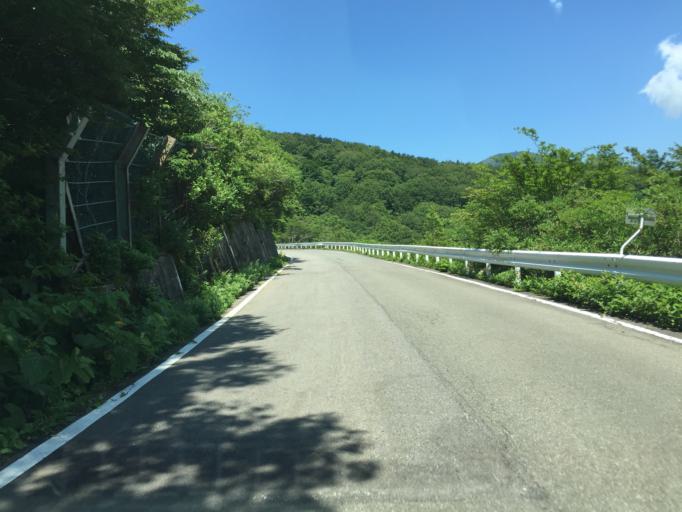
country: JP
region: Fukushima
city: Nihommatsu
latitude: 37.6642
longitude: 140.2816
